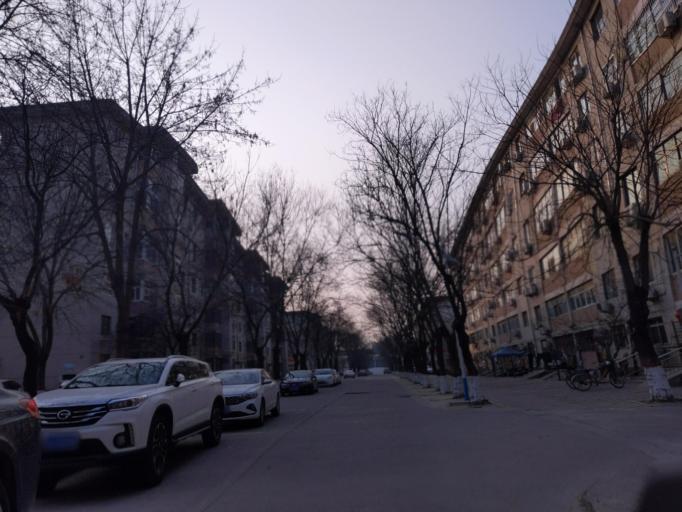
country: CN
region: Henan Sheng
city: Zhongyuanlu
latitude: 35.7820
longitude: 115.0586
